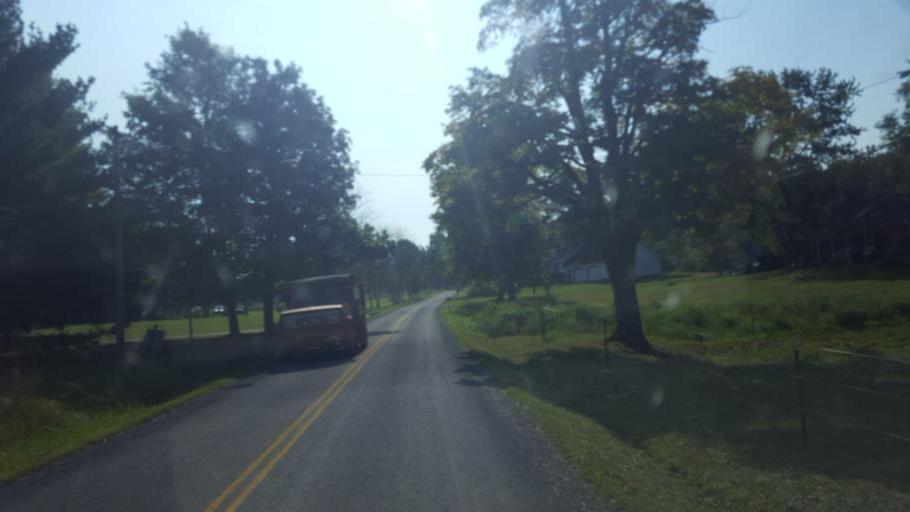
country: US
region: Ohio
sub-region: Ashtabula County
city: Orwell
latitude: 41.4678
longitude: -80.8763
